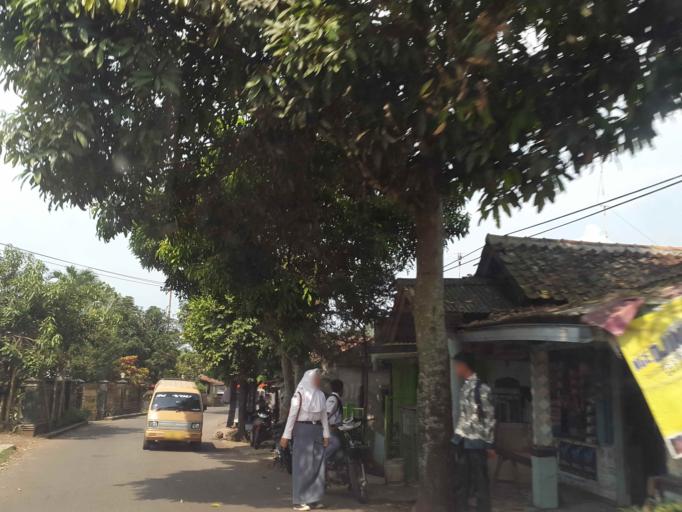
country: ID
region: West Java
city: Ciranjang-hilir
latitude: -6.7083
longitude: 107.1965
